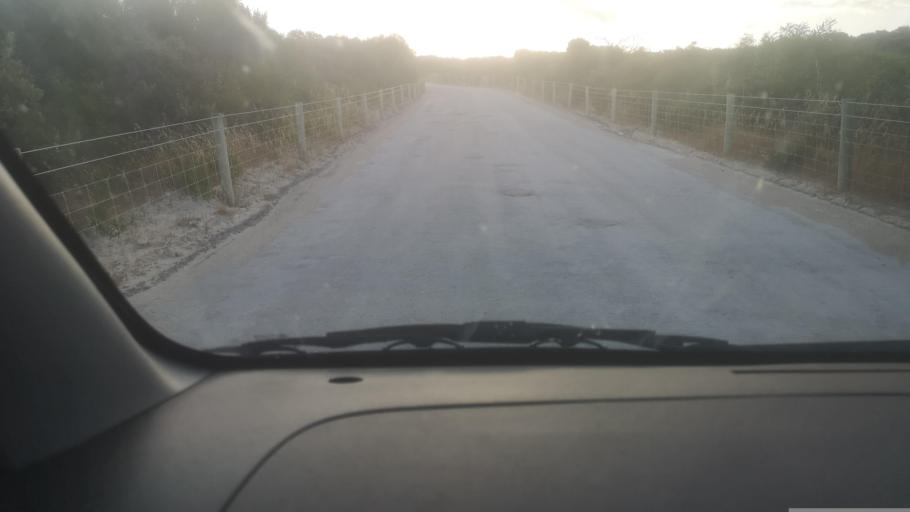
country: AU
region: Western Australia
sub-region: Wanneroo
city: Two Rocks
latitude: -31.5190
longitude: 115.6103
